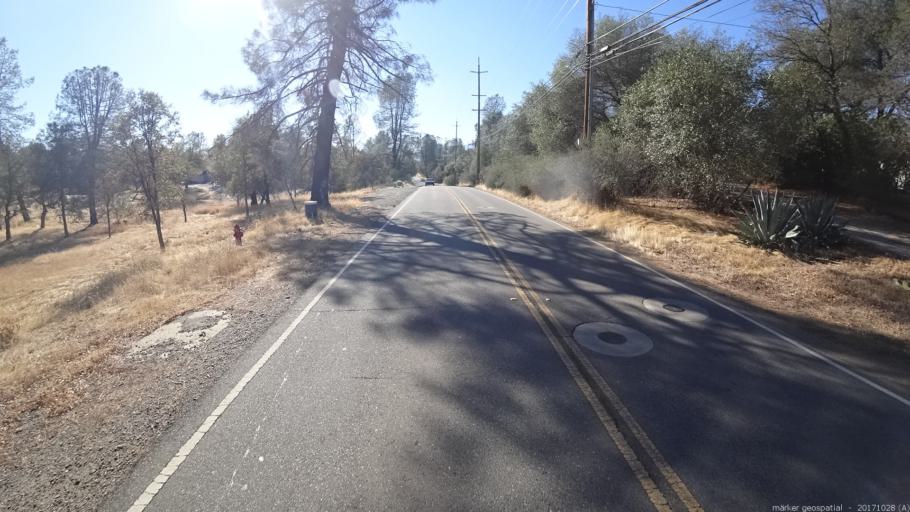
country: US
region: California
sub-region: Shasta County
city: Redding
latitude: 40.6241
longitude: -122.4187
